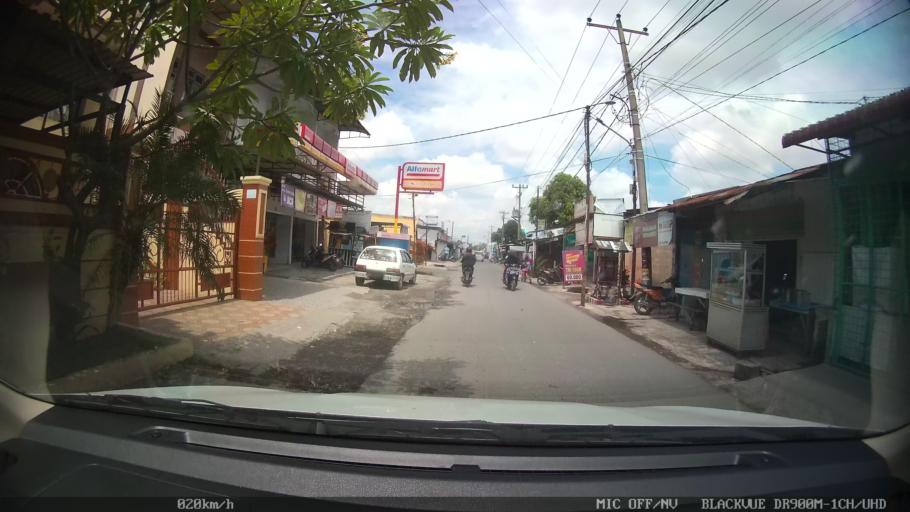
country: ID
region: North Sumatra
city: Medan
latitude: 3.6071
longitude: 98.7536
